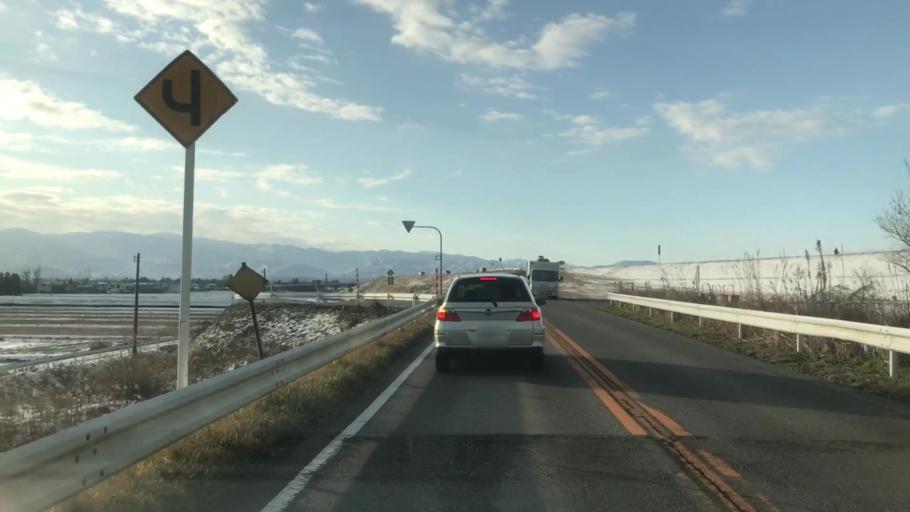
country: JP
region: Toyama
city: Toyama-shi
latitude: 36.6812
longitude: 137.2846
